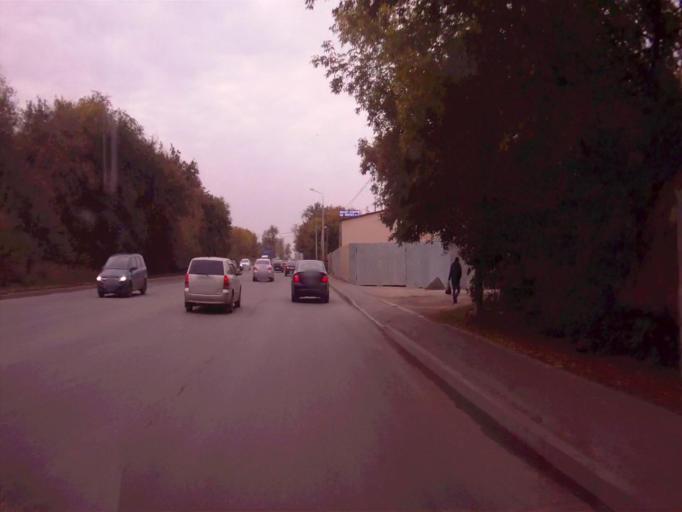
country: RU
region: Chelyabinsk
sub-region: Gorod Chelyabinsk
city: Chelyabinsk
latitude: 55.1297
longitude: 61.3853
